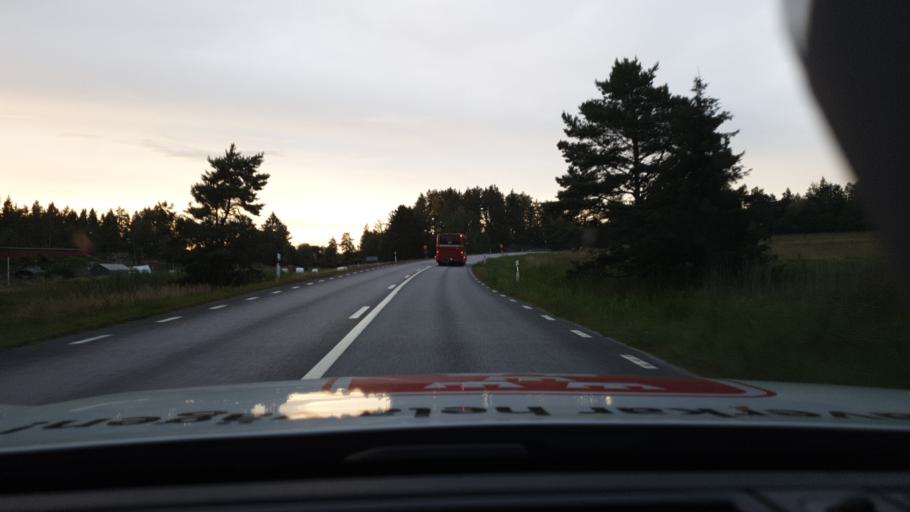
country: SE
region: Stockholm
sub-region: Norrtalje Kommun
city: Norrtalje
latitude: 59.6048
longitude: 18.6733
